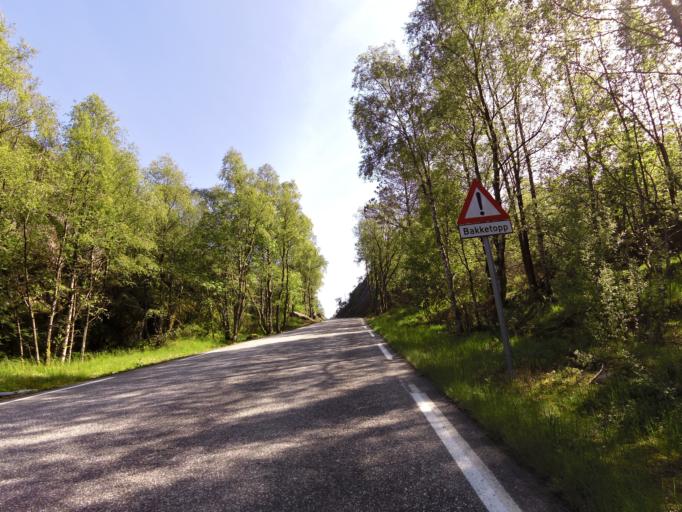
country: NO
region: Rogaland
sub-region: Sokndal
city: Hauge i Dalane
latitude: 58.3361
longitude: 6.3489
